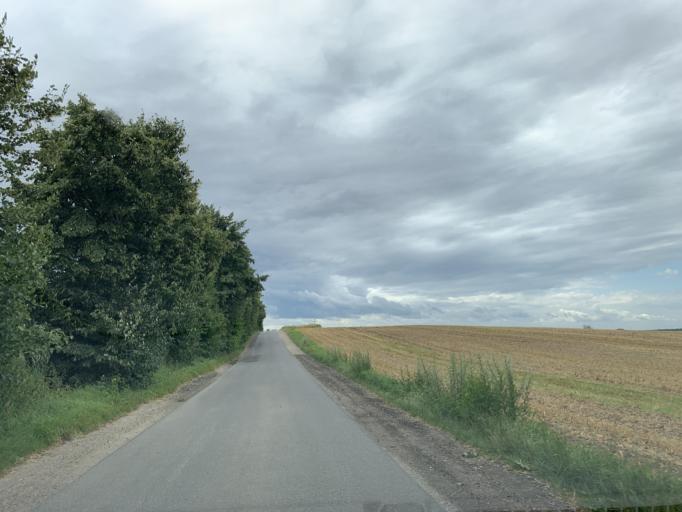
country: DE
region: Mecklenburg-Vorpommern
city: Burg Stargard
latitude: 53.4600
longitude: 13.2766
